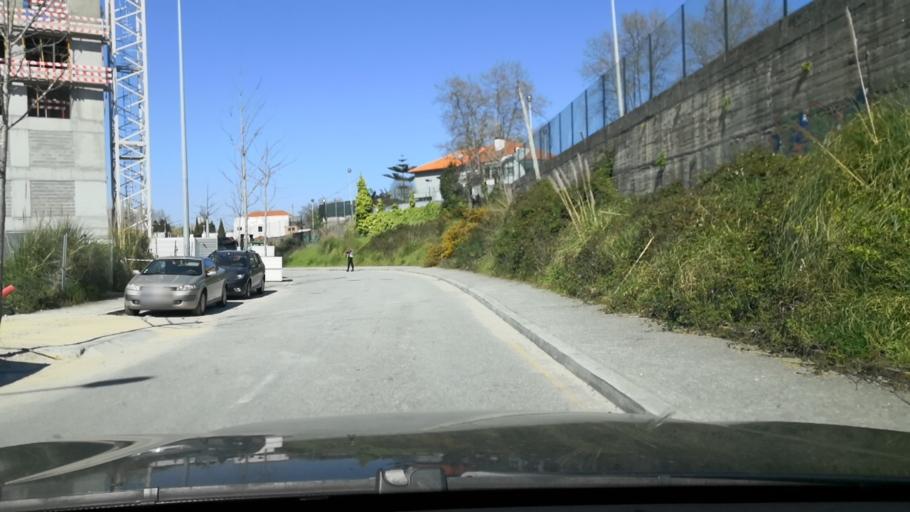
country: PT
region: Porto
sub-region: Porto
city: Porto
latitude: 41.1726
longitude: -8.6014
